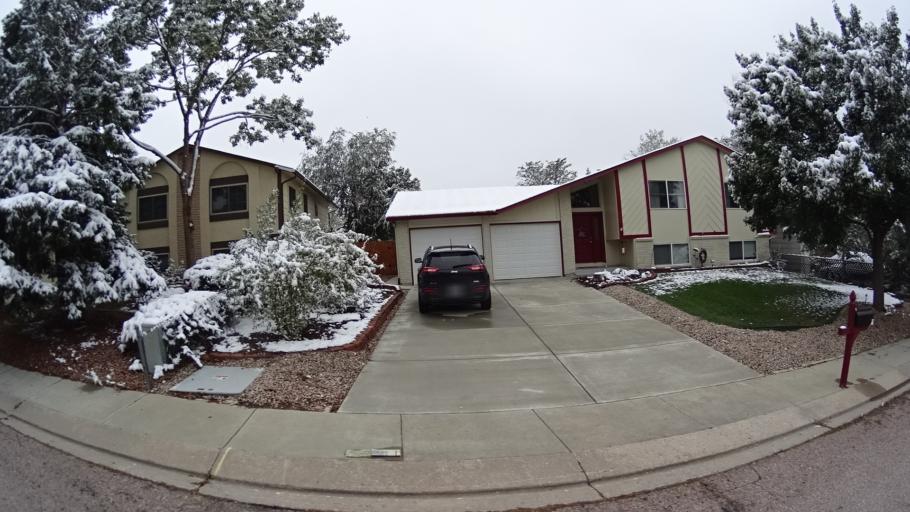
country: US
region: Colorado
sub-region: El Paso County
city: Colorado Springs
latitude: 38.9244
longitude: -104.7876
